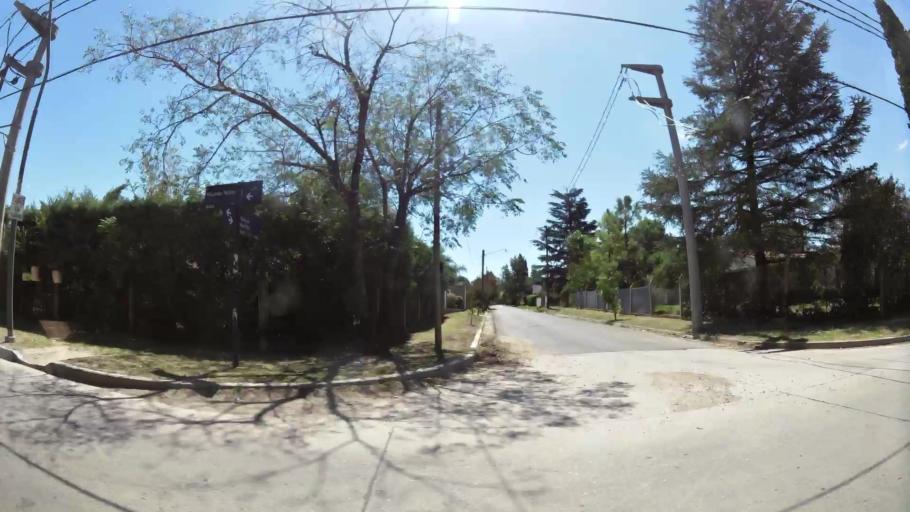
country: AR
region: Cordoba
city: Saldan
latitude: -31.3369
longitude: -64.2798
